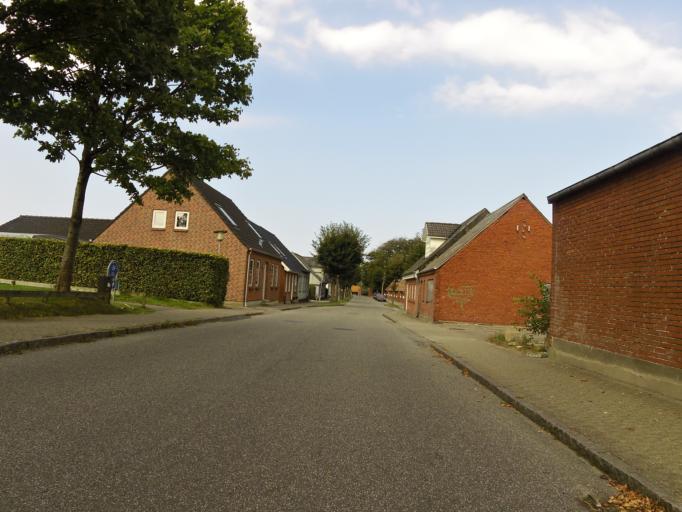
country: DK
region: South Denmark
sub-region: Vejen Kommune
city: Vejen
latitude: 55.4733
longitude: 9.1350
